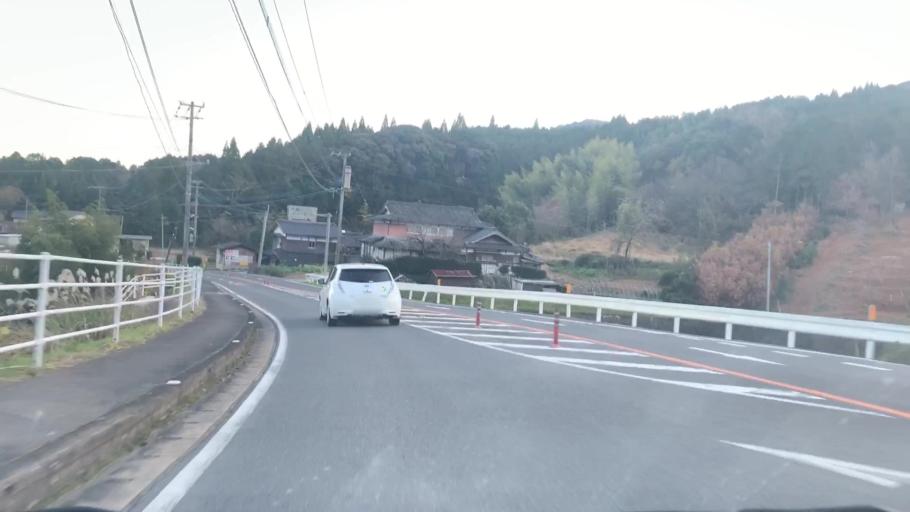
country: JP
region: Saga Prefecture
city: Takeocho-takeo
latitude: 33.2338
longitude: 130.0128
